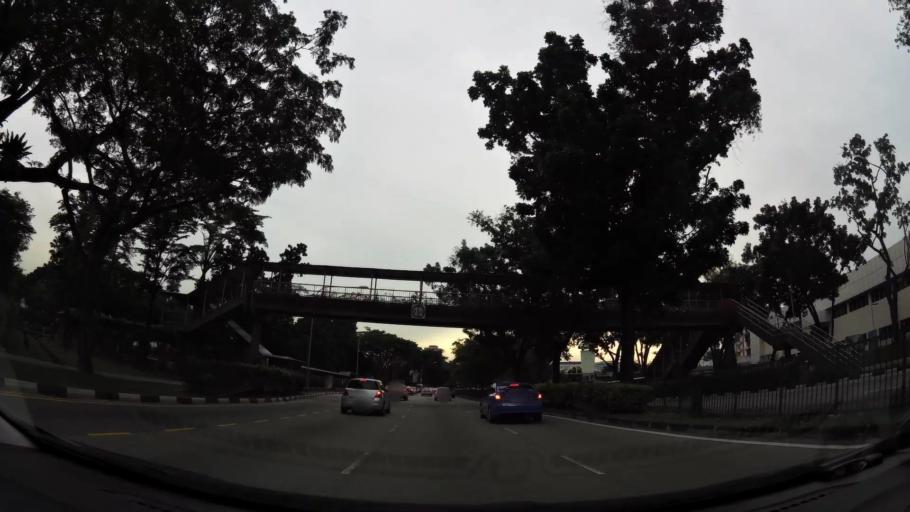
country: SG
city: Singapore
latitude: 1.3712
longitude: 103.8658
